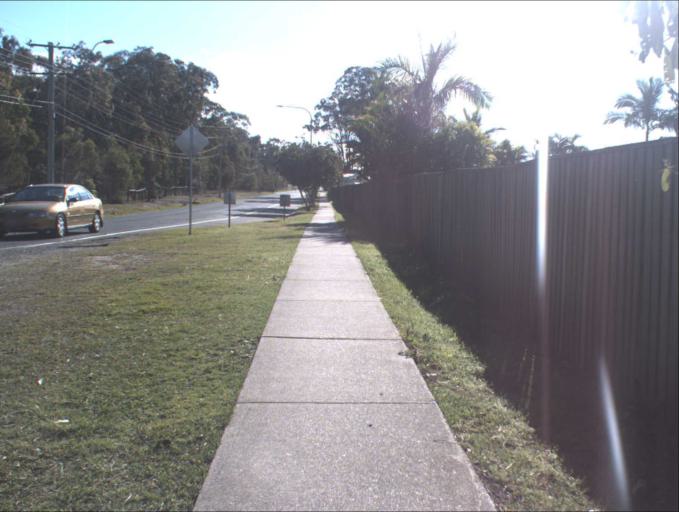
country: AU
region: Queensland
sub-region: Logan
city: Logan Reserve
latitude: -27.6982
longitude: 153.0875
